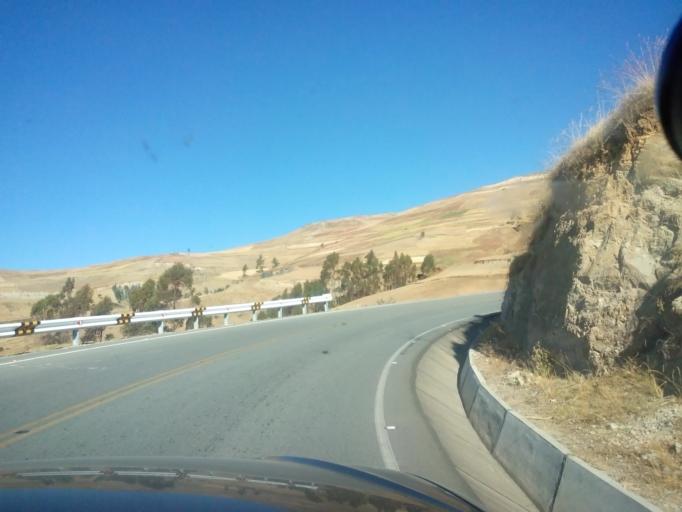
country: PE
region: Apurimac
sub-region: Provincia de Andahuaylas
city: Pacucha
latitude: -13.6588
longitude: -73.2888
